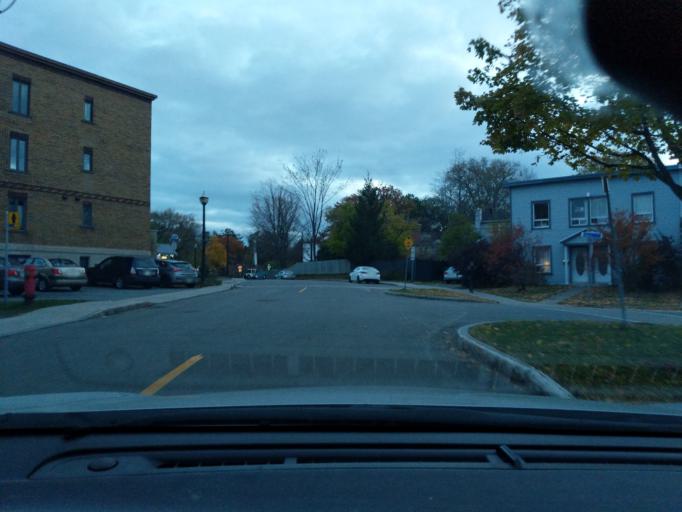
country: CA
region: Quebec
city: Quebec
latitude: 46.7823
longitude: -71.2481
